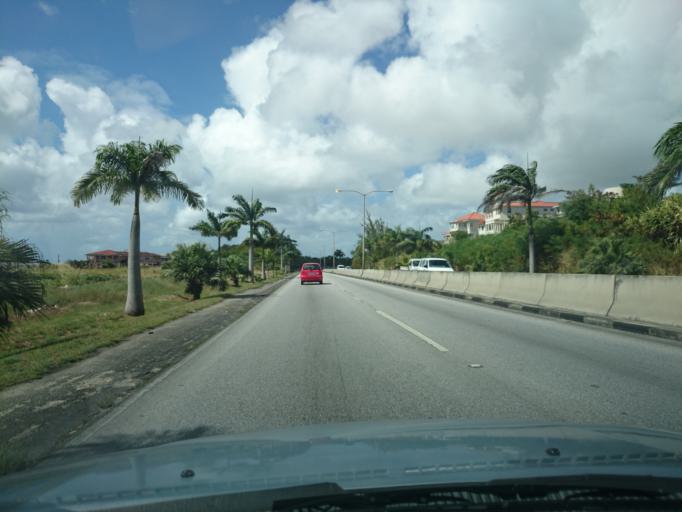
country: BB
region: Christ Church
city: Oistins
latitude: 13.0798
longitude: -59.5727
